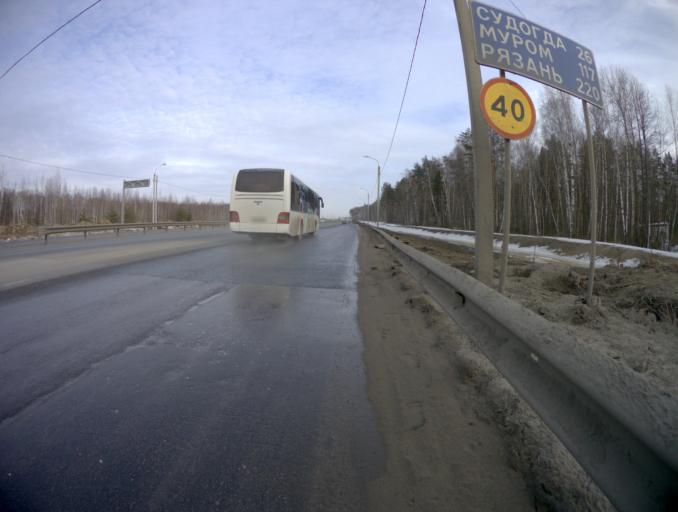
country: RU
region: Vladimir
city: Kommunar
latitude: 56.0773
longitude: 40.4779
